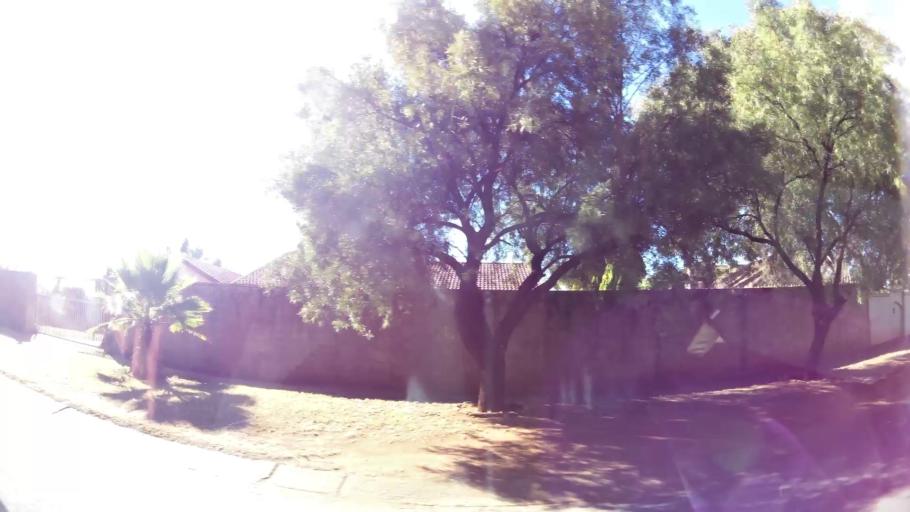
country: ZA
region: Gauteng
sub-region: West Rand District Municipality
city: Carletonville
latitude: -26.3584
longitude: 27.3735
